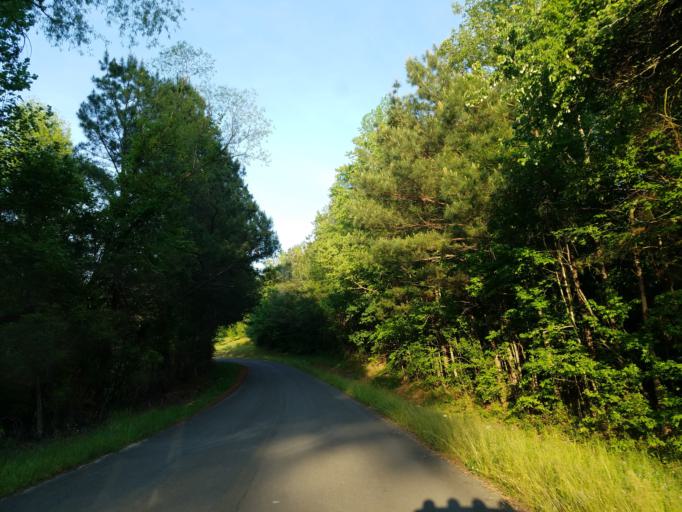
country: US
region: Georgia
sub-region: Whitfield County
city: Dalton
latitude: 34.6488
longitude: -85.0865
